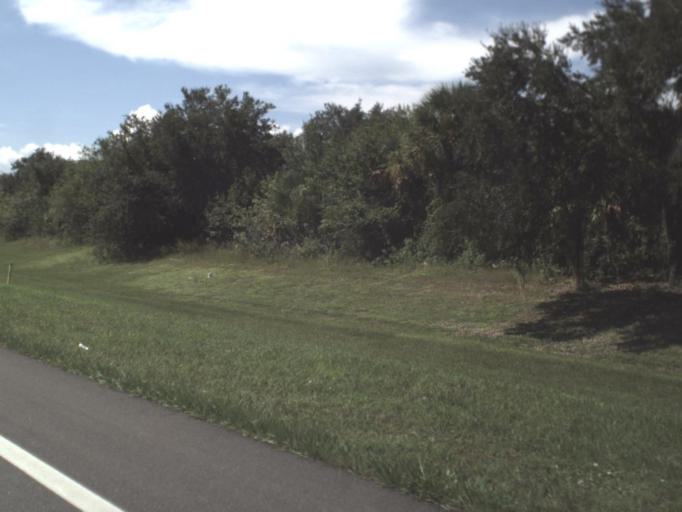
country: US
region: Florida
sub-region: Sarasota County
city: North Port
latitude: 27.0242
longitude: -82.1638
